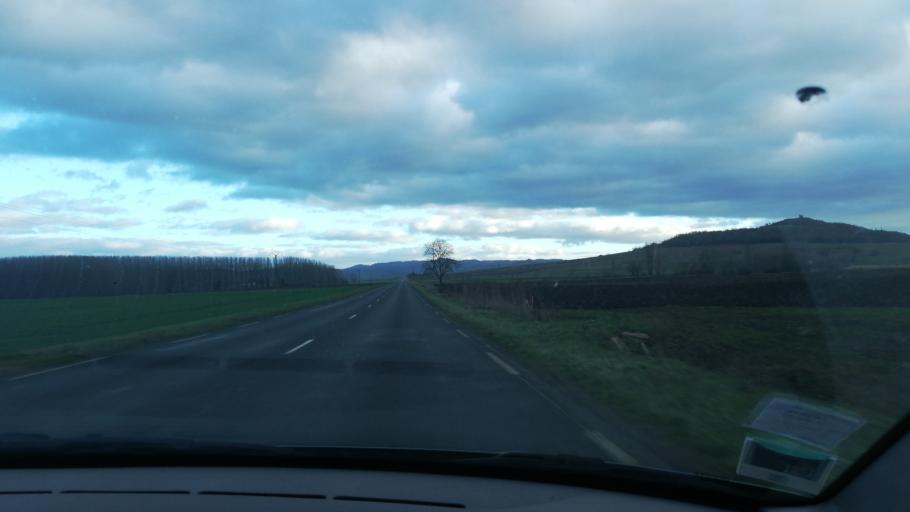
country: FR
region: Auvergne
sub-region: Departement du Puy-de-Dome
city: Vertaizon
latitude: 45.7602
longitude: 3.3097
